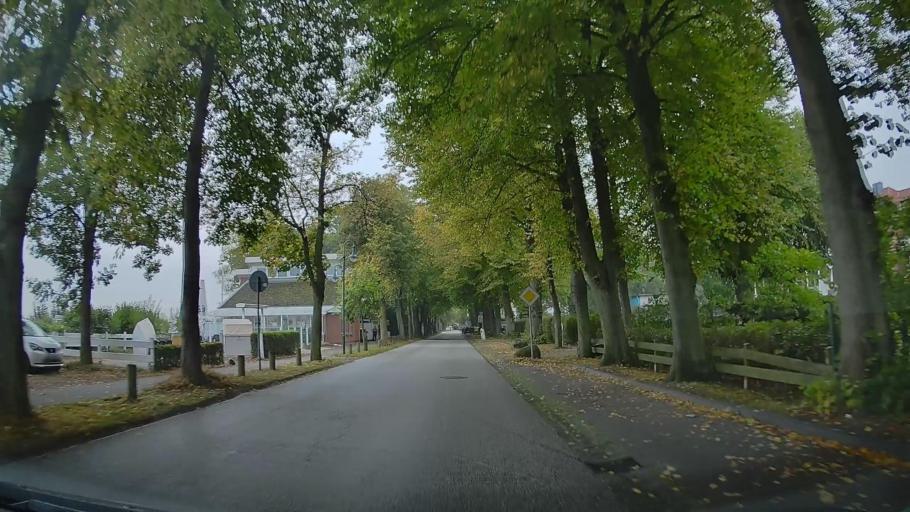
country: DE
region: Mecklenburg-Vorpommern
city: Ostseebad Boltenhagen
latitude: 53.9918
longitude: 11.1993
